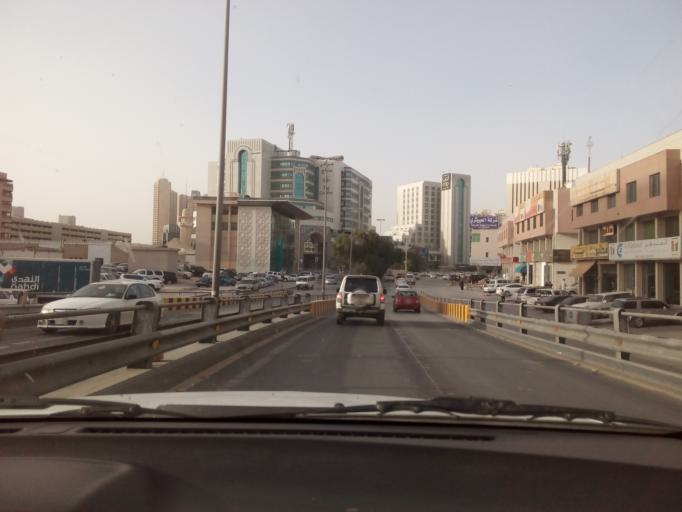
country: SA
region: Ar Riyad
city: Riyadh
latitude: 24.6310
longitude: 46.7167
